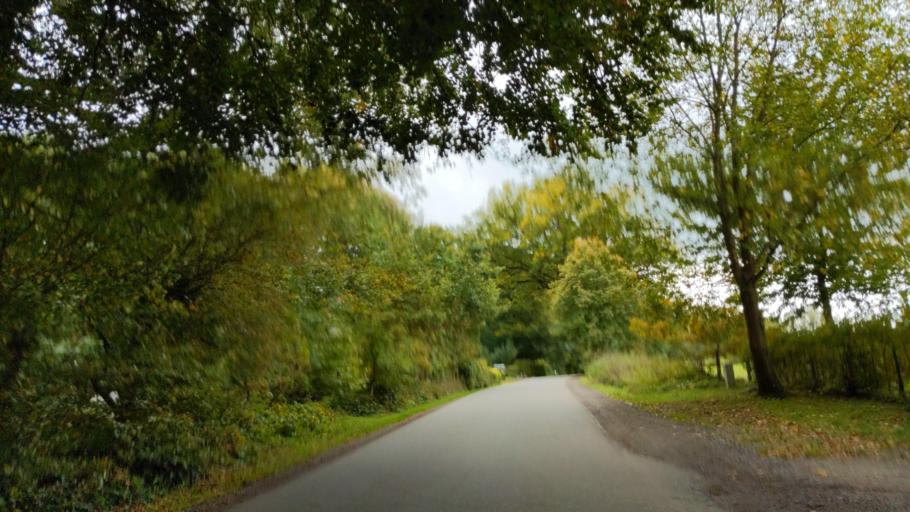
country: DE
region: Schleswig-Holstein
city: Neustadt in Holstein
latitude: 54.1343
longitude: 10.7838
